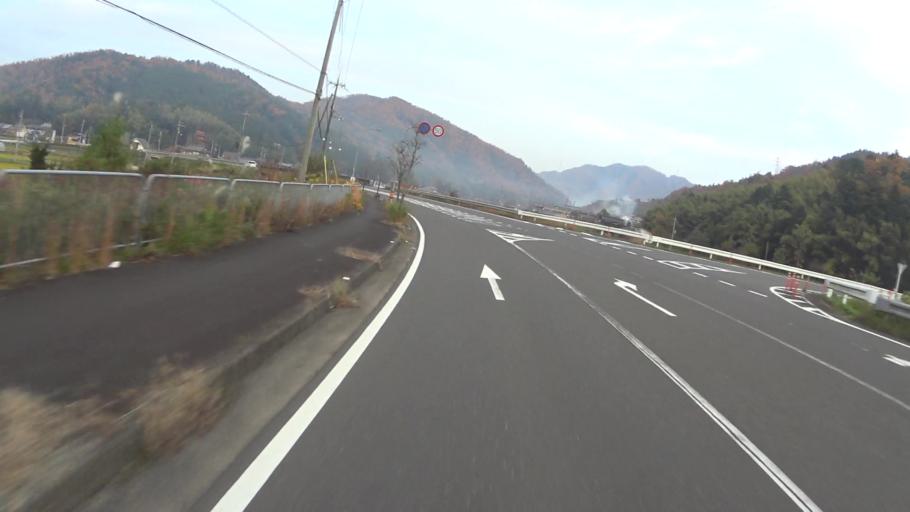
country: JP
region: Kyoto
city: Maizuru
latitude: 35.4623
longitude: 135.4207
